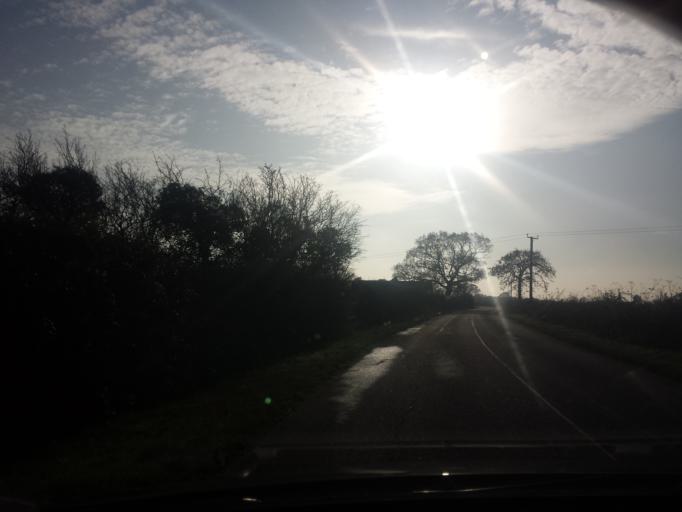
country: GB
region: England
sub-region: Essex
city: Little Clacton
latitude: 51.8260
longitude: 1.1123
